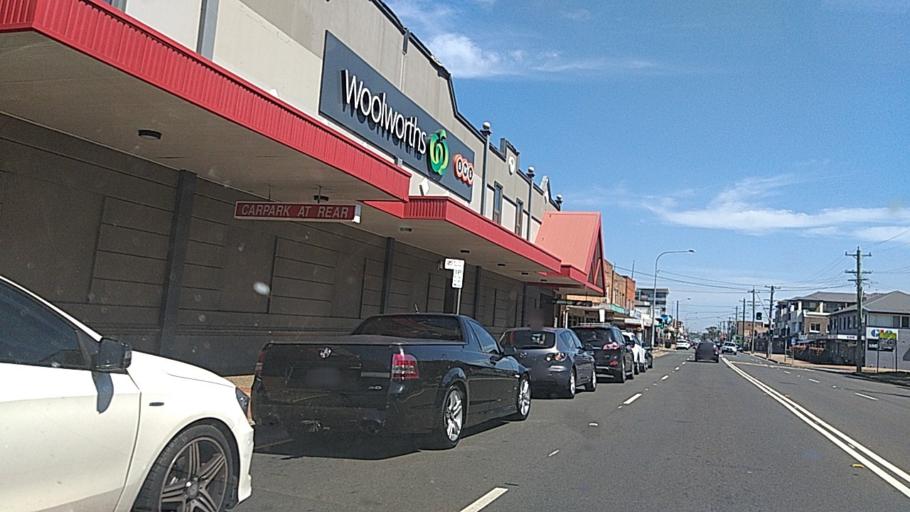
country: AU
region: New South Wales
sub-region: Wollongong
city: Fairy Meadow
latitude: -34.3913
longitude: 150.8934
